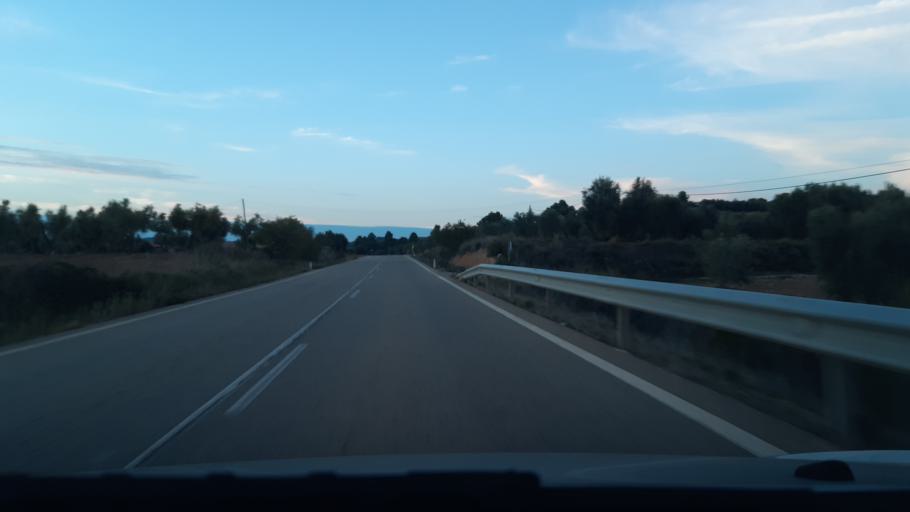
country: ES
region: Aragon
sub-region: Provincia de Teruel
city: Valderrobres
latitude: 40.8524
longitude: 0.1737
